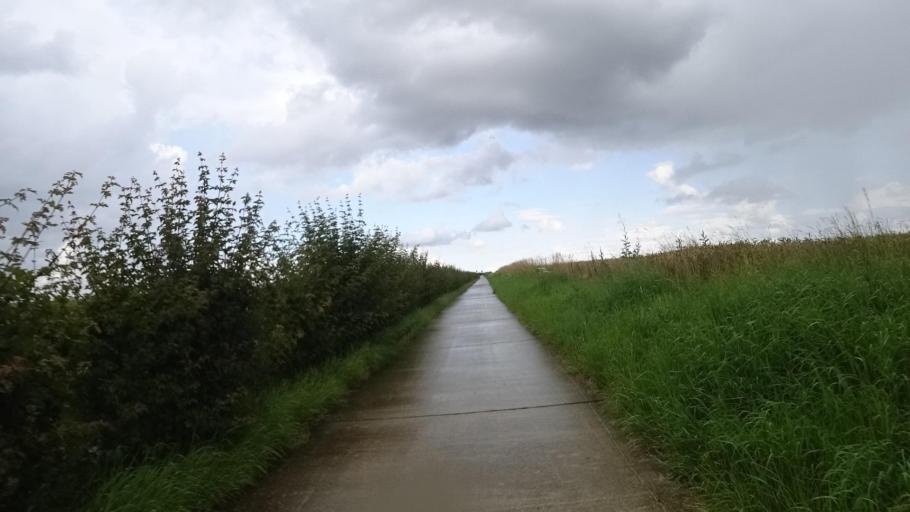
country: BE
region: Wallonia
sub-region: Province du Brabant Wallon
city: Chastre
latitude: 50.5833
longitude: 4.6161
